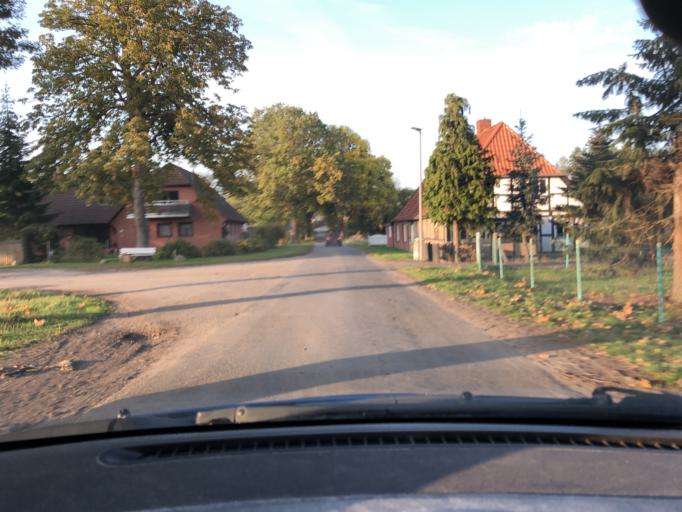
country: DE
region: Lower Saxony
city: Hitzacker
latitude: 53.1482
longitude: 11.0041
